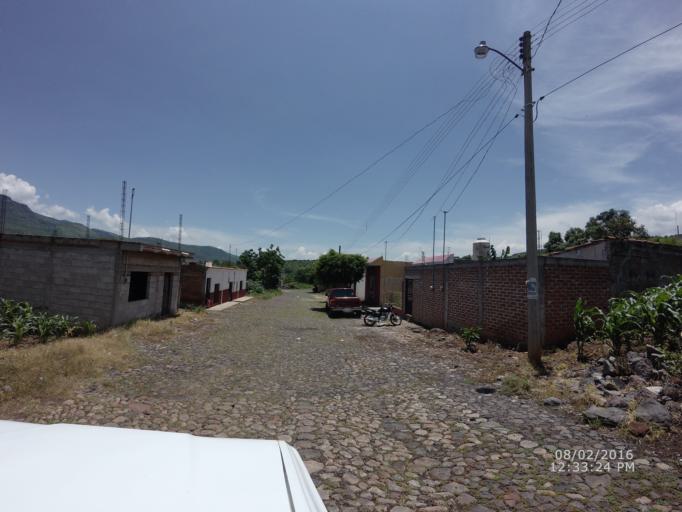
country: MX
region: Nayarit
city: Ixtlan del Rio
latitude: 21.0311
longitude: -104.3515
